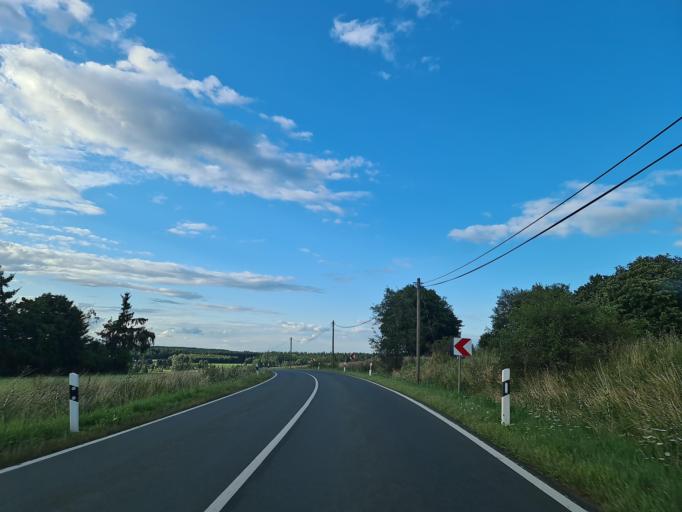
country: DE
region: Saxony
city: Pausa
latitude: 50.5917
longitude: 11.9978
